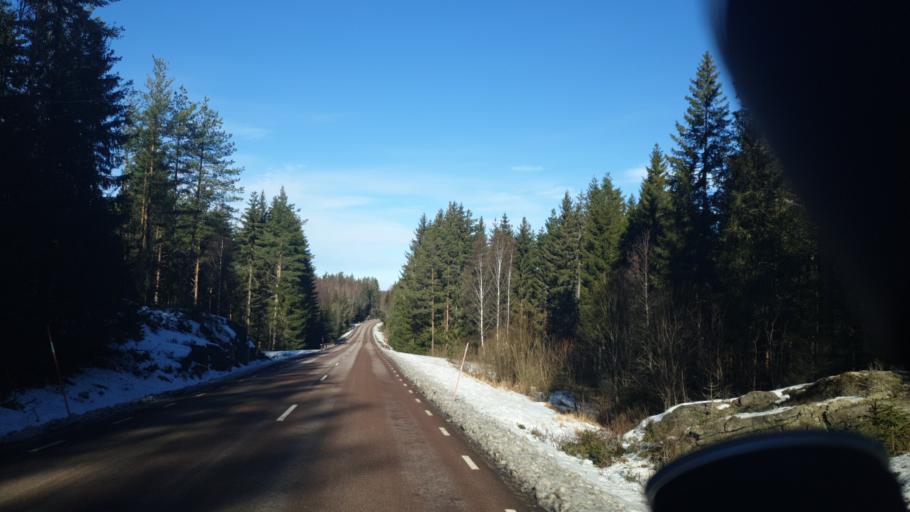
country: SE
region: Vaermland
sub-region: Grums Kommun
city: Grums
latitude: 59.4027
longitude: 13.0134
